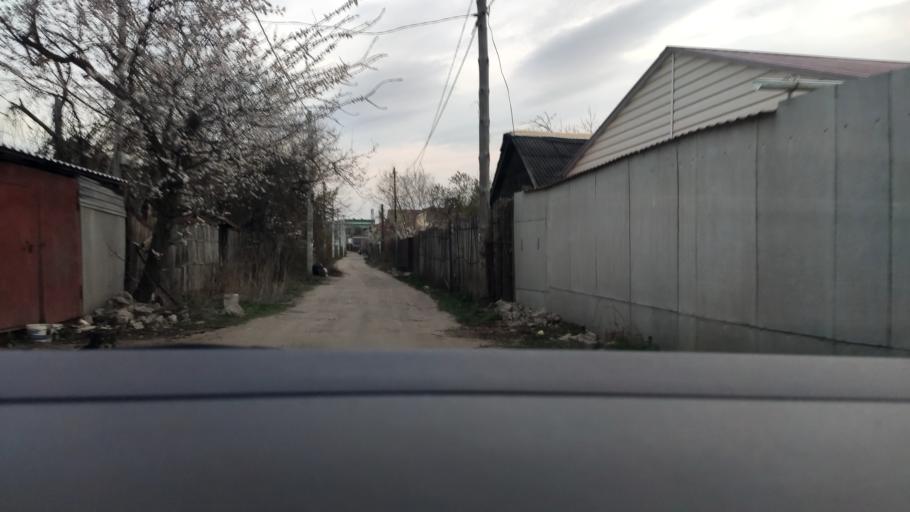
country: RU
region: Voronezj
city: Maslovka
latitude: 51.6010
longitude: 39.2322
